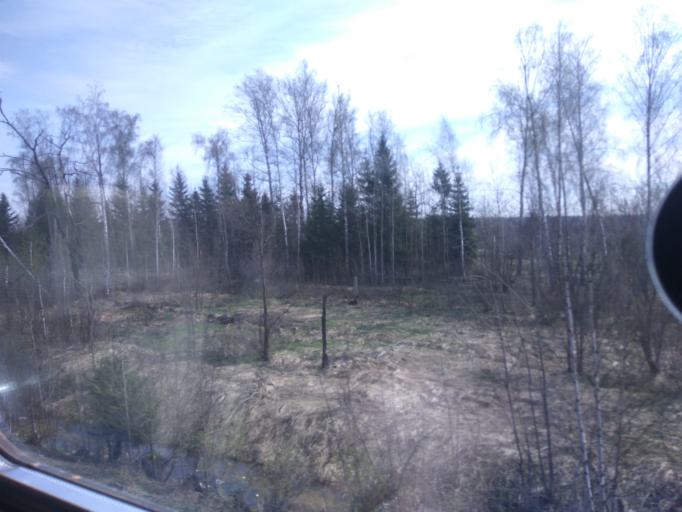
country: RU
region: Moskovskaya
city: Lugovaya
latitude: 56.0327
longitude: 37.4882
